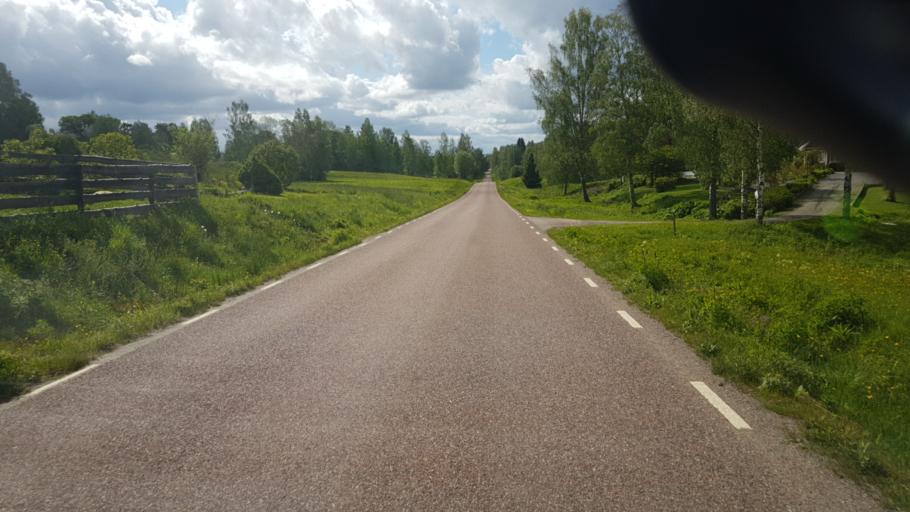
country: NO
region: Ostfold
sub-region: Romskog
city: Romskog
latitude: 59.7367
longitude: 12.0596
